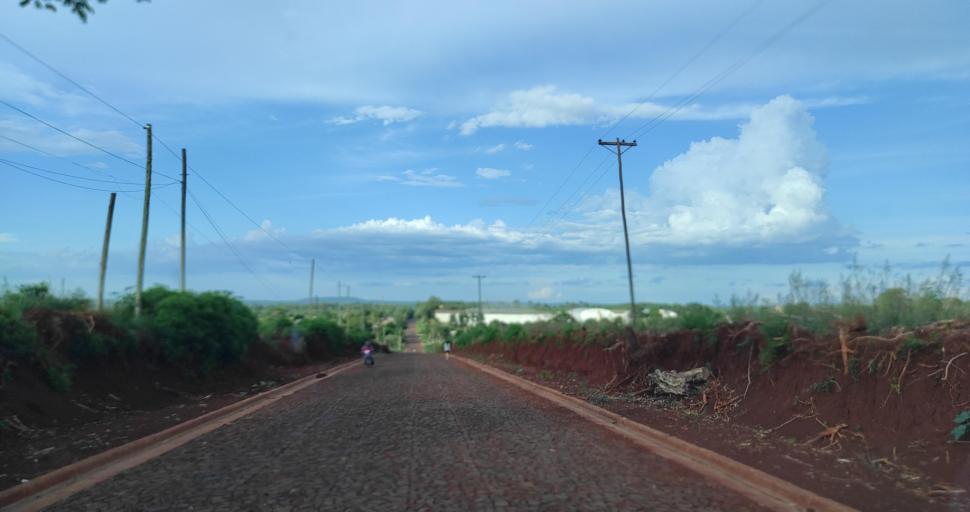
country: AR
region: Misiones
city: Santo Pipo
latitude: -27.1417
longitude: -55.4180
